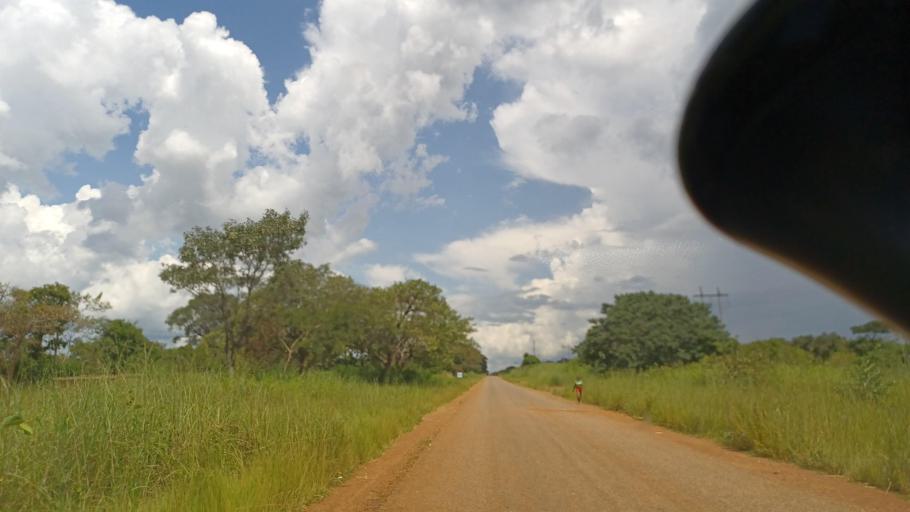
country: ZM
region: North-Western
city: Kasempa
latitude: -12.7864
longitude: 26.0116
